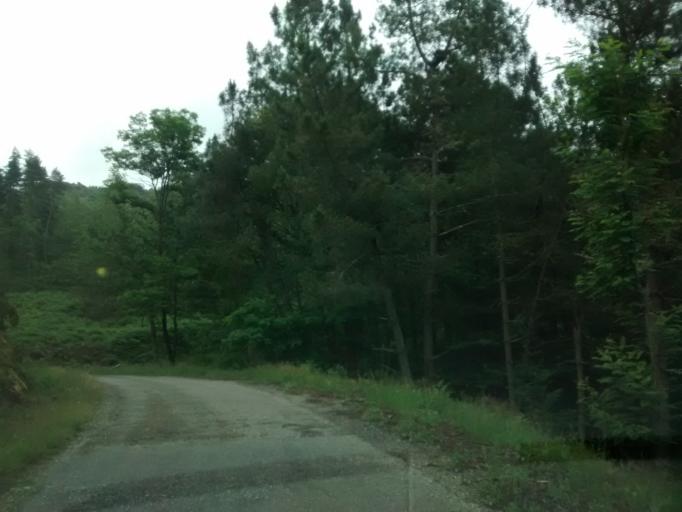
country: ES
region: Galicia
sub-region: Provincia de Ourense
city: Castro Caldelas
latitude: 42.4080
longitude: -7.3937
